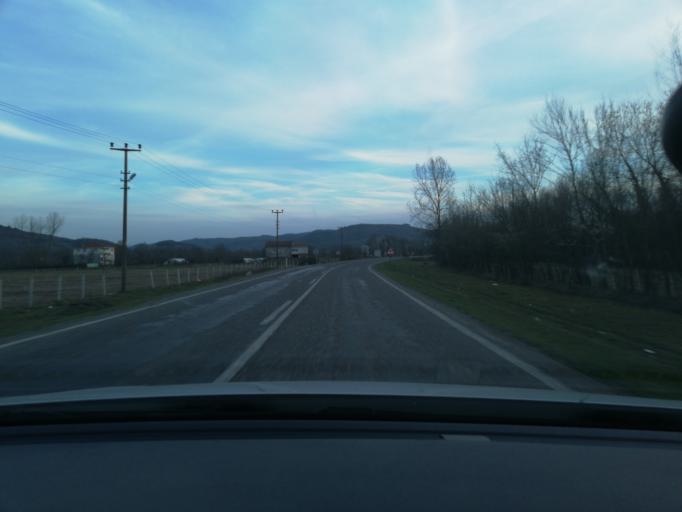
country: TR
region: Zonguldak
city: Saltukova
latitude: 41.5149
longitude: 32.1030
